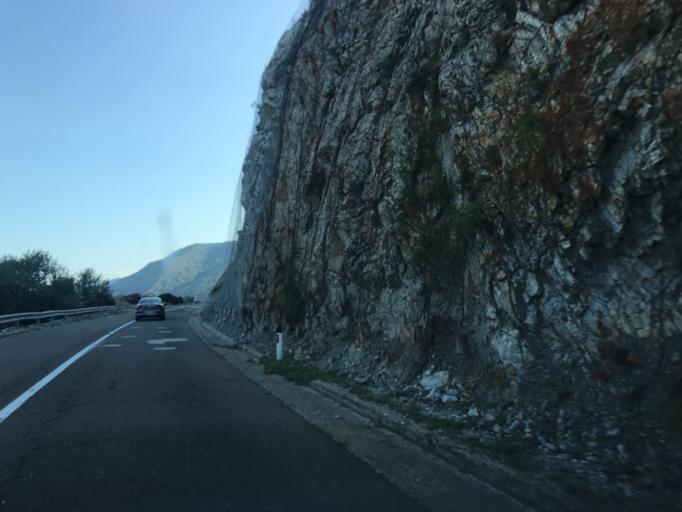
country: RO
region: Caras-Severin
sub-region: Comuna Berzasca
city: Berzasca
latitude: 44.5891
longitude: 22.0224
